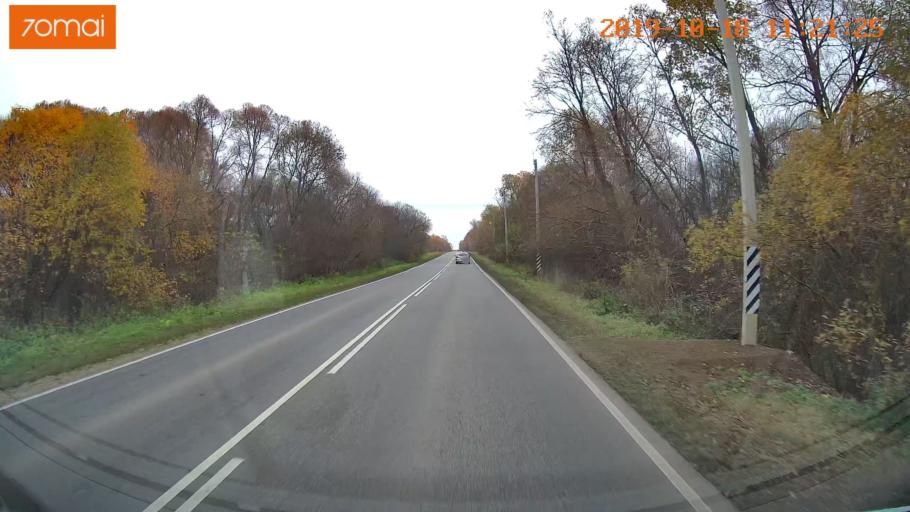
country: RU
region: Tula
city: Kimovsk
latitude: 54.0737
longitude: 38.5647
